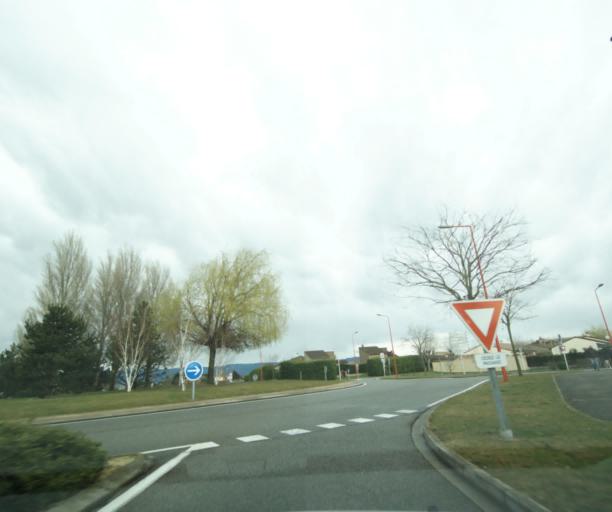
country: FR
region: Rhone-Alpes
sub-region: Departement de la Drome
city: Bourg-les-Valence
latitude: 44.9603
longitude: 4.9093
